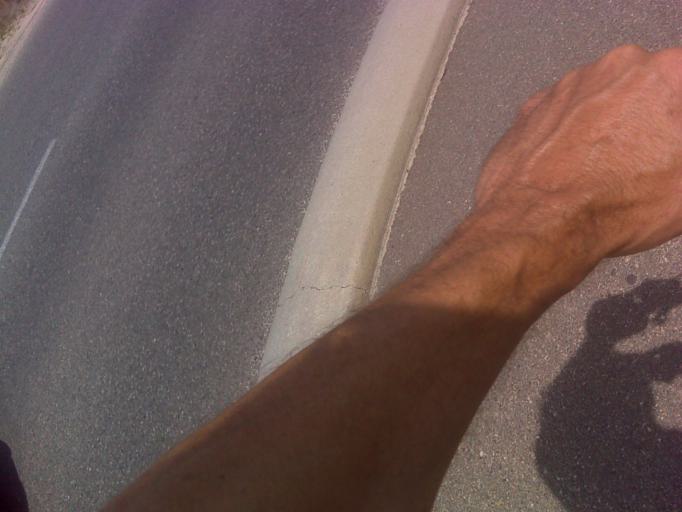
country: FR
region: Aquitaine
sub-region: Departement des Landes
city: Capbreton
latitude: 43.6702
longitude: -1.4393
